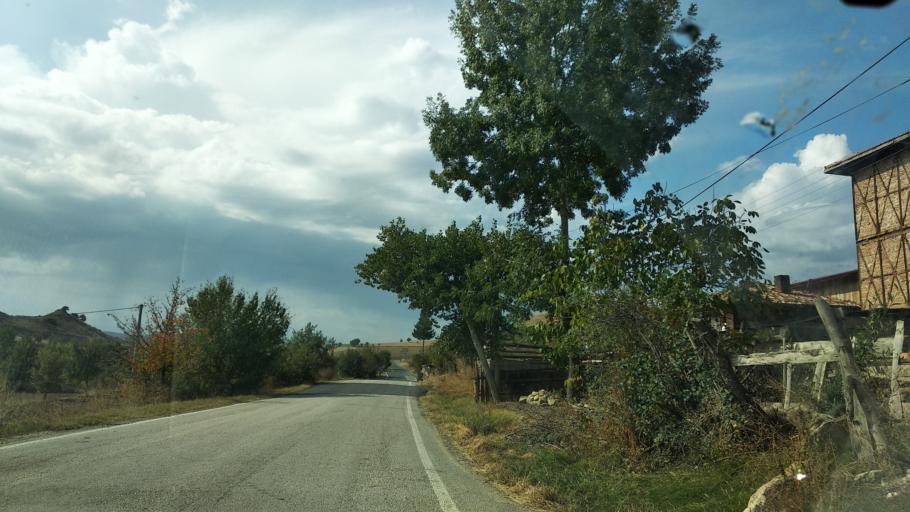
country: TR
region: Bolu
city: Seben
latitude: 40.4040
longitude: 31.5672
